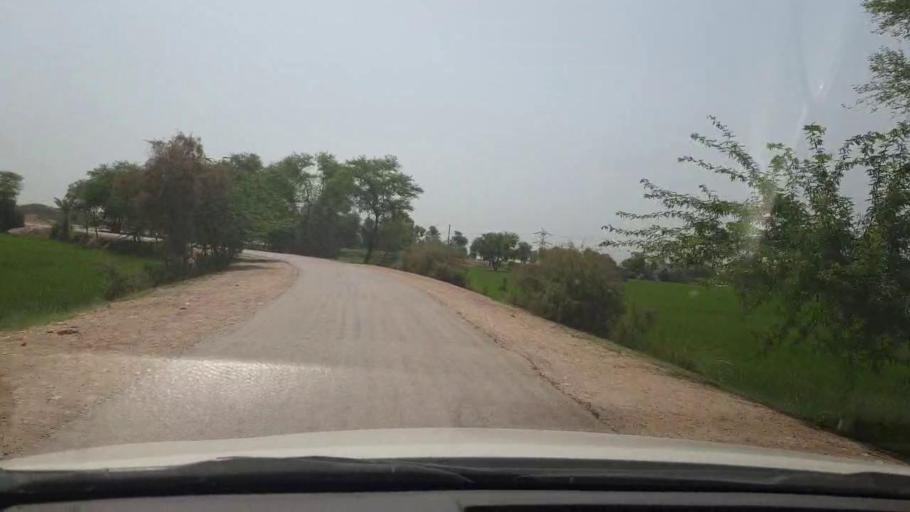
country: PK
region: Sindh
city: Shikarpur
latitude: 28.0186
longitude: 68.6610
